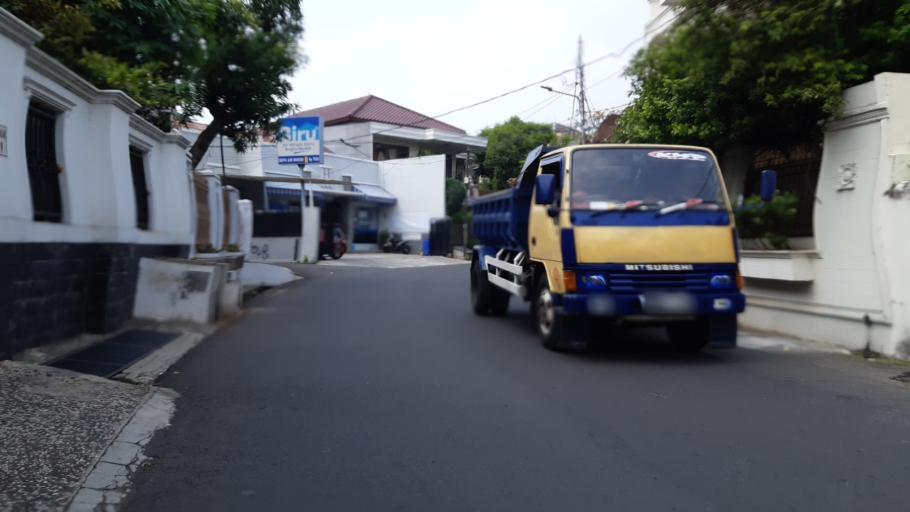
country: ID
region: Jakarta Raya
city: Jakarta
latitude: -6.2388
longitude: 106.8575
